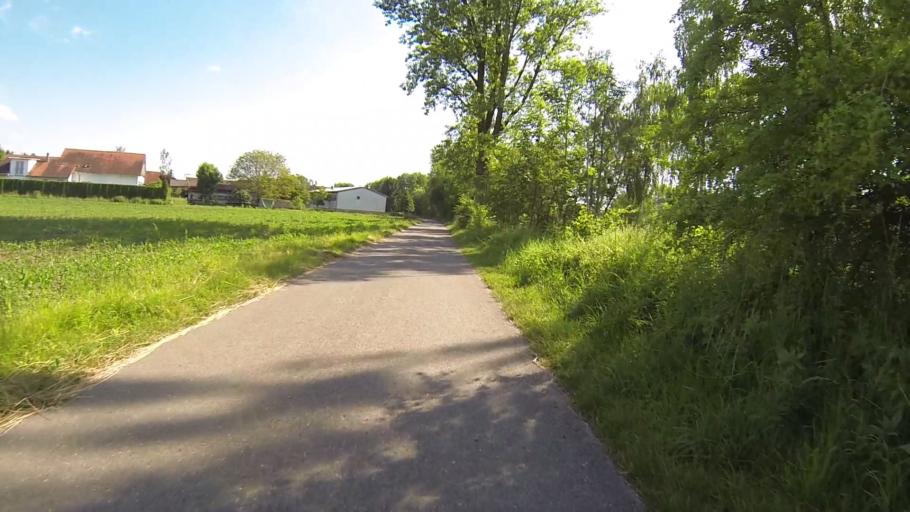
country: DE
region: Baden-Wuerttemberg
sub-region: Tuebingen Region
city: Laupheim
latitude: 48.1925
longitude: 9.8278
